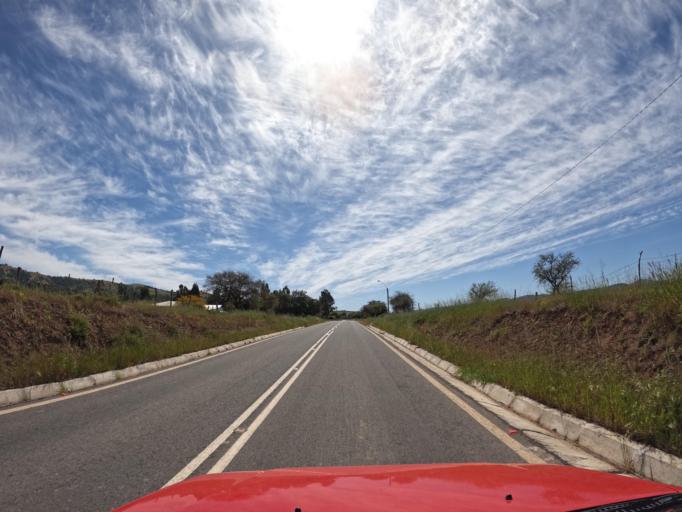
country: CL
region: Maule
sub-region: Provincia de Talca
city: Talca
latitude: -35.0311
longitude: -71.7627
